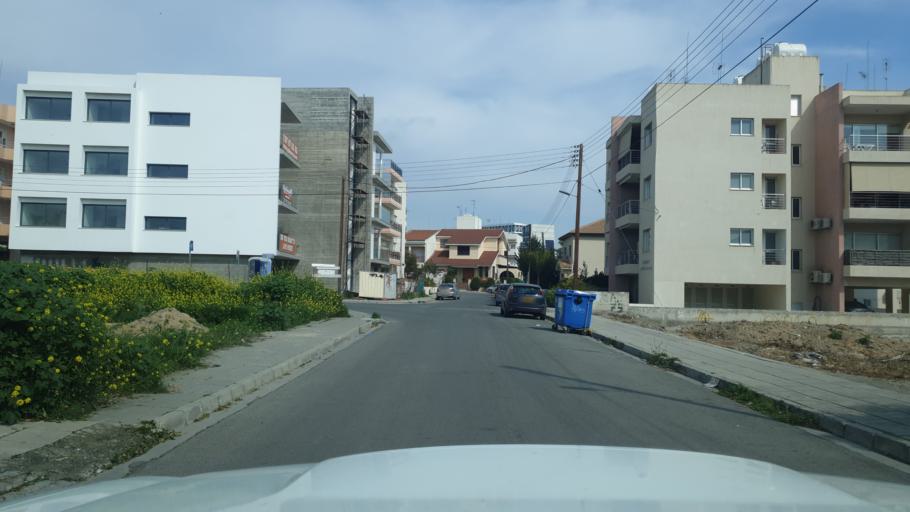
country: CY
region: Lefkosia
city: Nicosia
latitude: 35.1641
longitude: 33.3154
